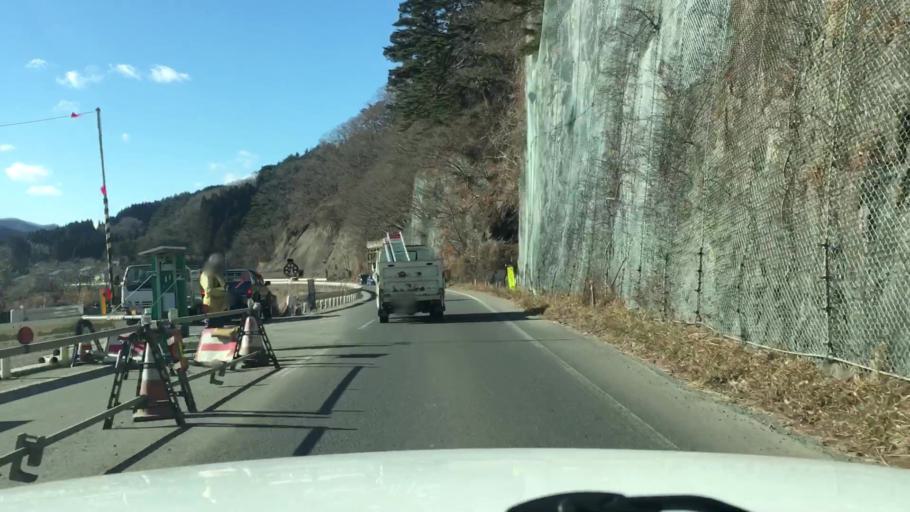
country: JP
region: Iwate
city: Miyako
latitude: 39.6323
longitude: 141.8666
